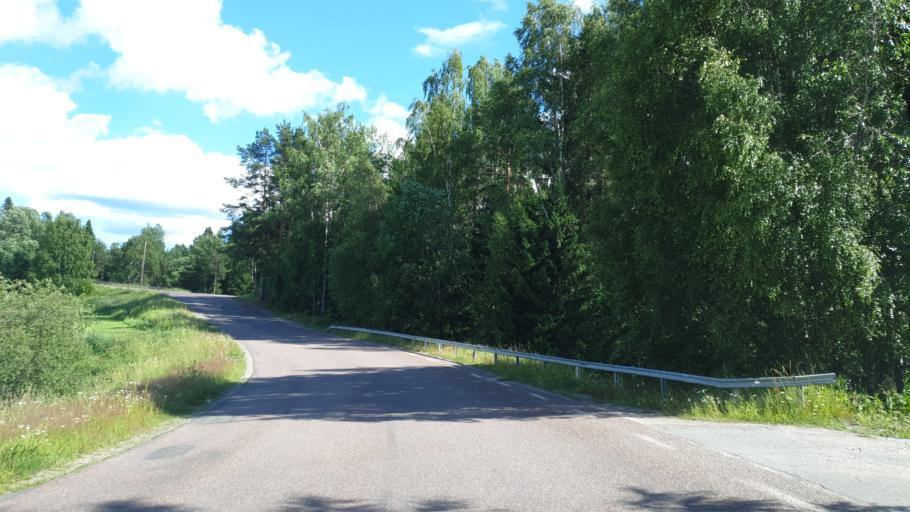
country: SE
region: Gaevleborg
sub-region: Nordanstigs Kommun
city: Bergsjoe
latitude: 62.0476
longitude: 17.2387
